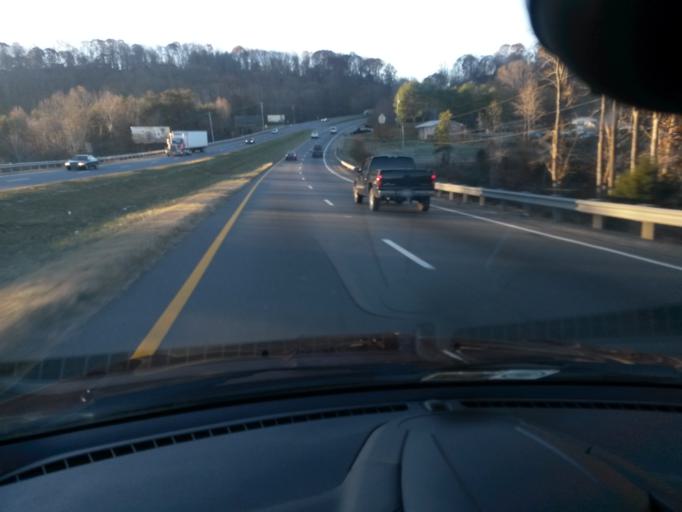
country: US
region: Virginia
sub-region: Franklin County
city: Rocky Mount
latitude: 37.0400
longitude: -79.8752
